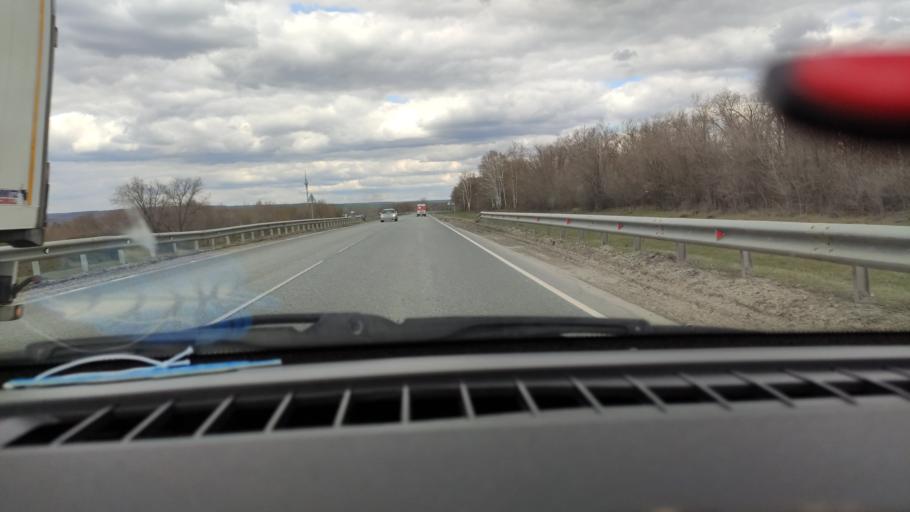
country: RU
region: Saratov
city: Tersa
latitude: 52.0900
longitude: 47.5460
